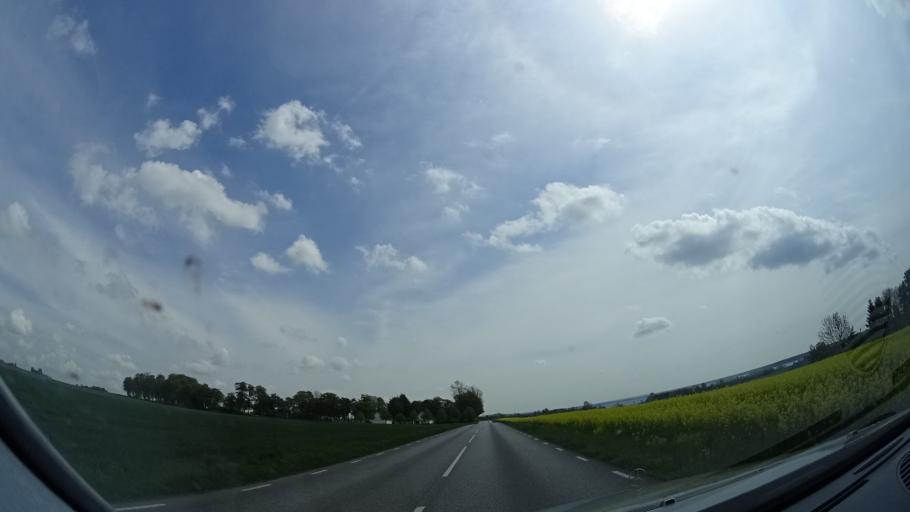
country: SE
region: Skane
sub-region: Hoors Kommun
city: Loberod
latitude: 55.7116
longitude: 13.5445
